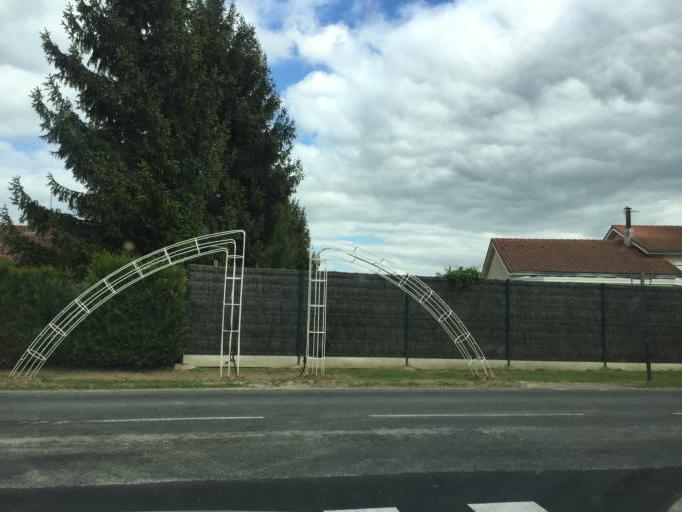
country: FR
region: Rhone-Alpes
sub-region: Departement de l'Ain
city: Saint-Andre-de-Corcy
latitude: 45.9582
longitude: 4.9406
